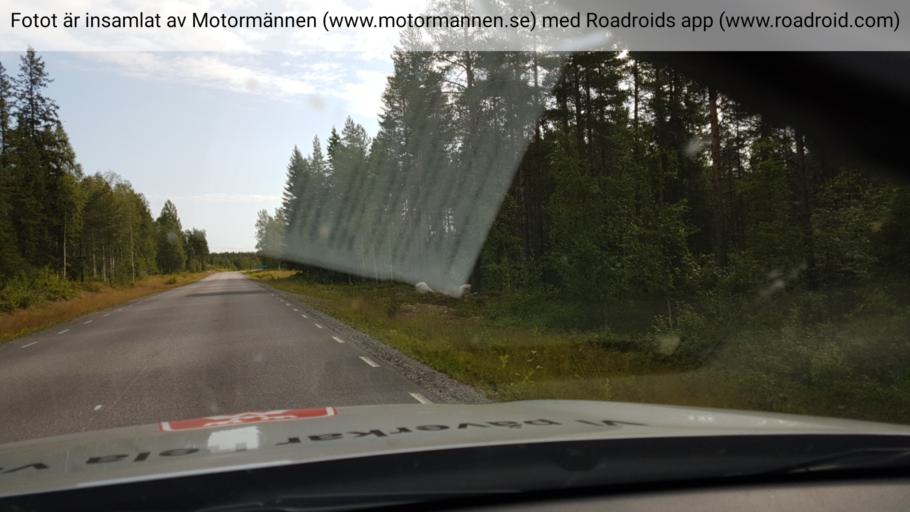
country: SE
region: Vaesterbotten
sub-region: Skelleftea Kommun
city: Storvik
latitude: 65.5178
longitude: 20.5498
